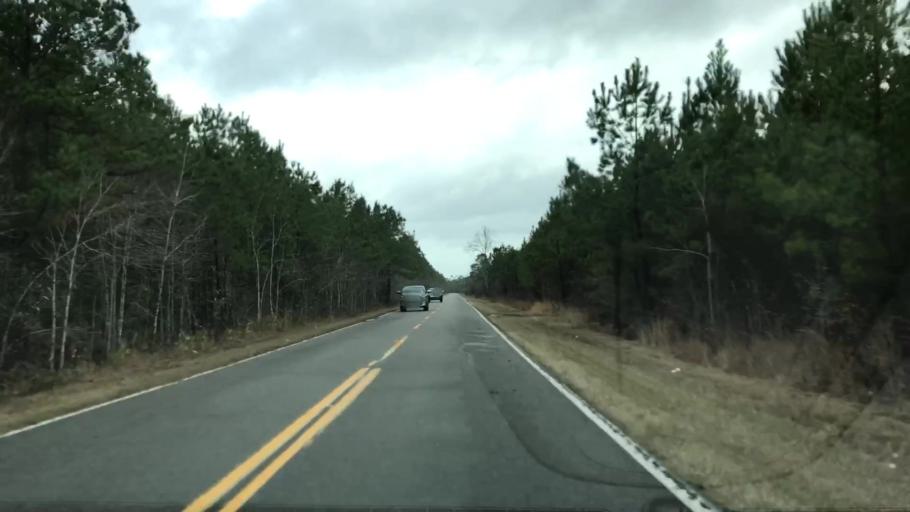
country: US
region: South Carolina
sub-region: Georgetown County
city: Murrells Inlet
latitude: 33.6267
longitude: -79.2419
